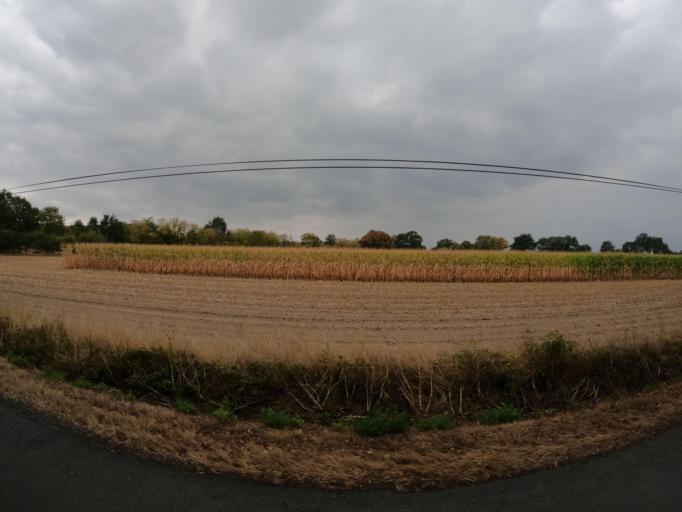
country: FR
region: Pays de la Loire
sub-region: Departement de la Vendee
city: La Boissiere-de-Montaigu
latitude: 46.9768
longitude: -1.1967
